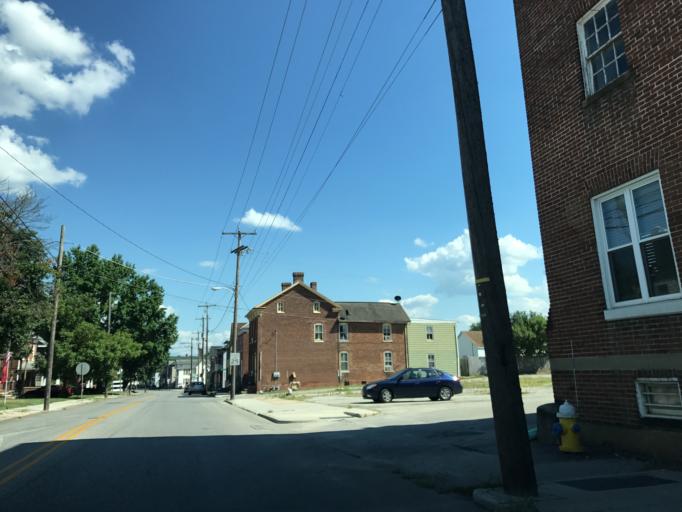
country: US
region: Pennsylvania
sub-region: York County
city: Hanover
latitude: 39.8019
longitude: -76.9896
